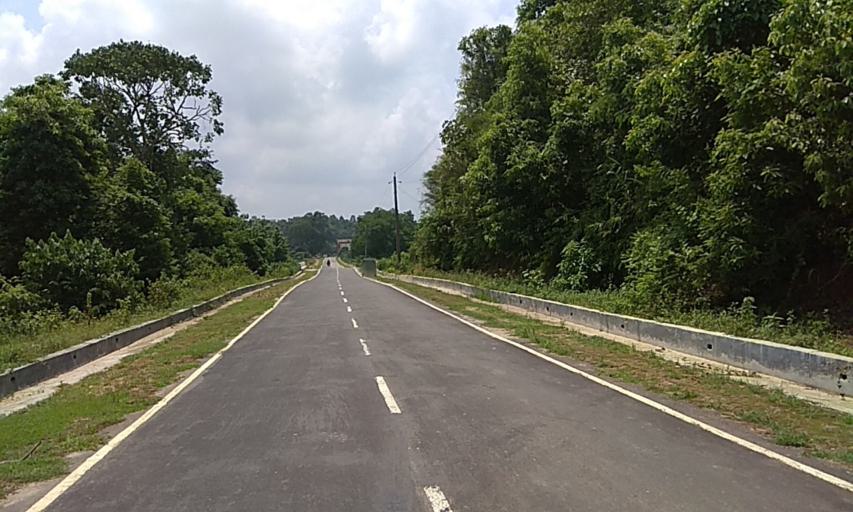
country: BD
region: Chittagong
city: Manikchari
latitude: 22.9367
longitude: 91.9070
